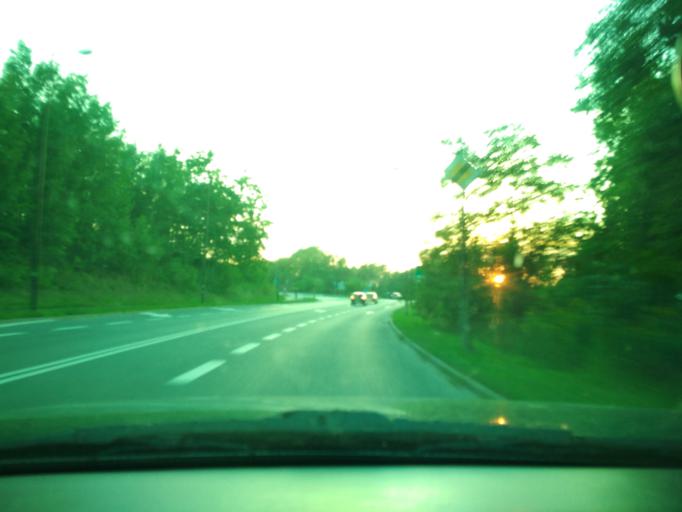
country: PL
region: Silesian Voivodeship
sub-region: Gliwice
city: Gliwice
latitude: 50.2713
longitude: 18.6879
